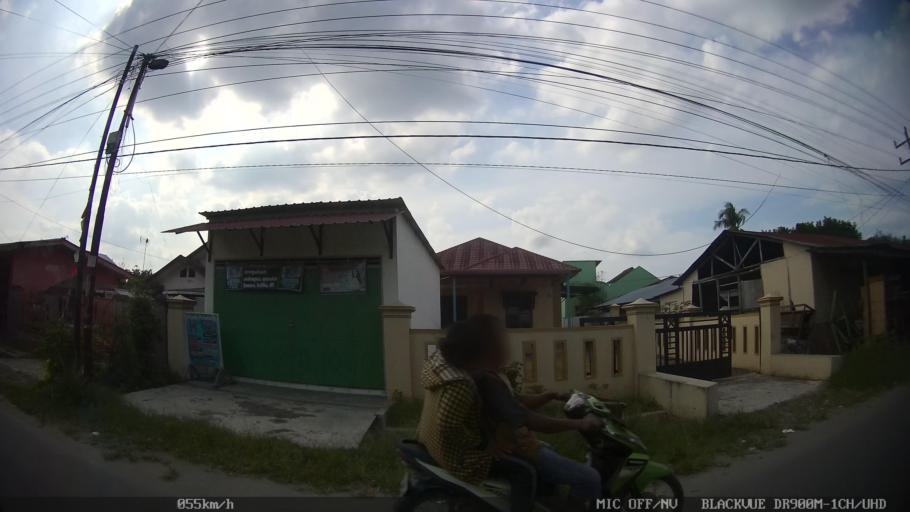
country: ID
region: North Sumatra
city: Binjai
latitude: 3.6399
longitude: 98.4943
